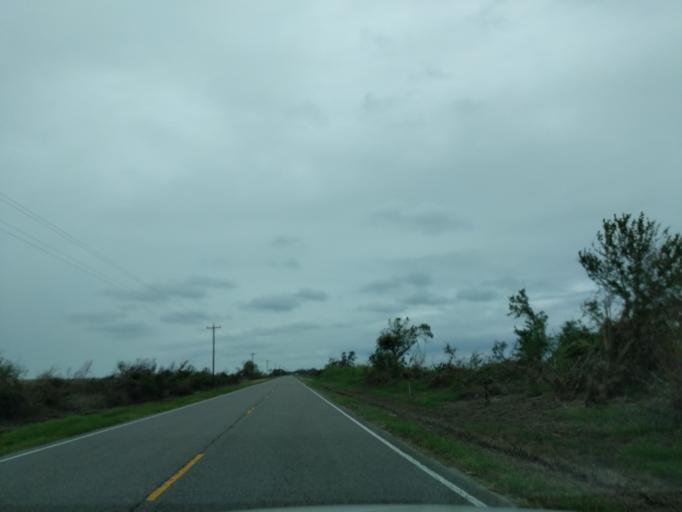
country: US
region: Louisiana
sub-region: Cameron Parish
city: Cameron
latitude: 29.7867
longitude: -93.1607
